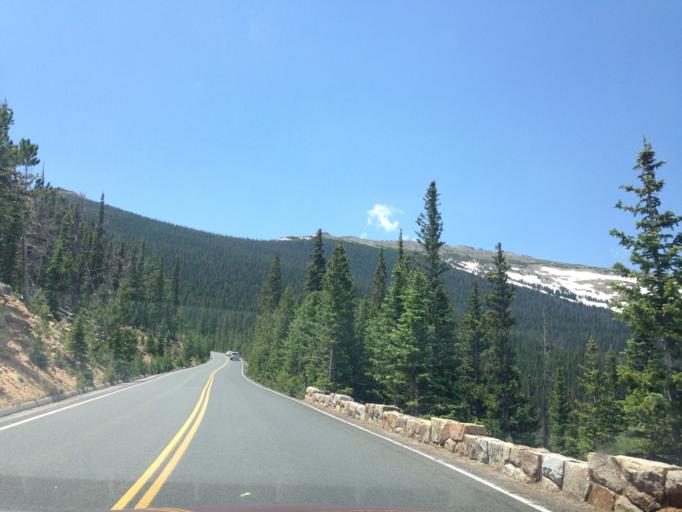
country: US
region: Colorado
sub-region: Larimer County
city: Estes Park
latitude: 40.3901
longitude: -105.6518
